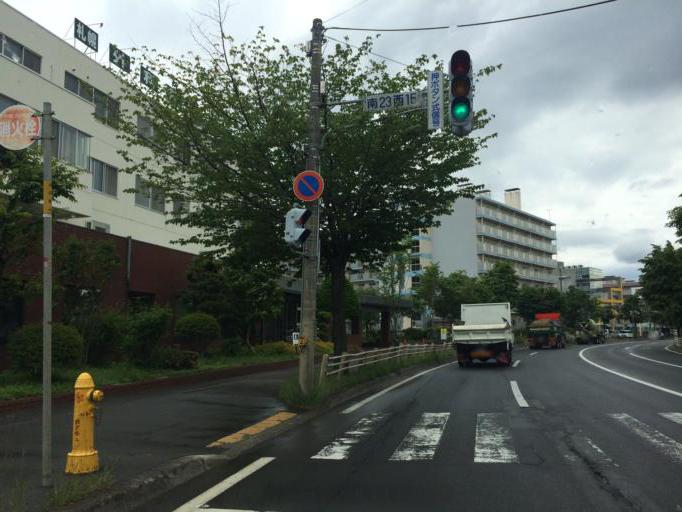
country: JP
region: Hokkaido
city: Sapporo
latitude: 43.0273
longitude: 141.3384
